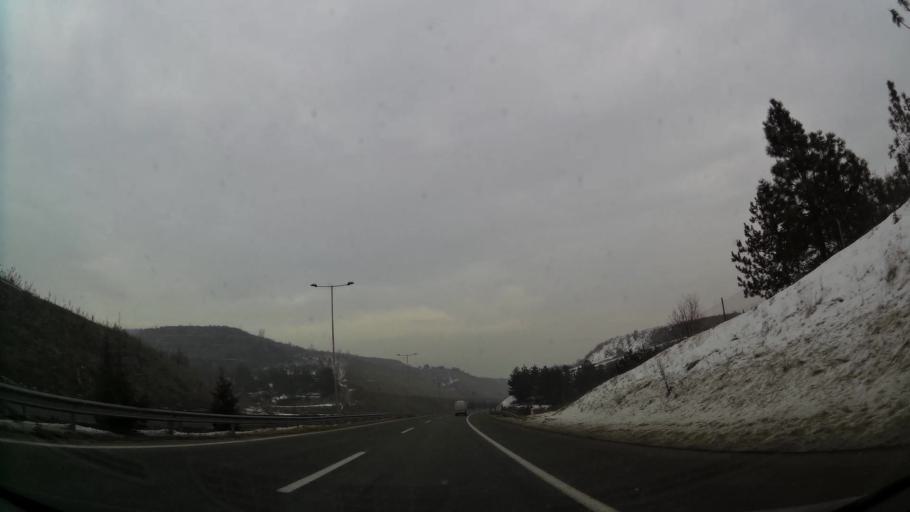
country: MK
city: Kondovo
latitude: 42.0534
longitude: 21.3404
